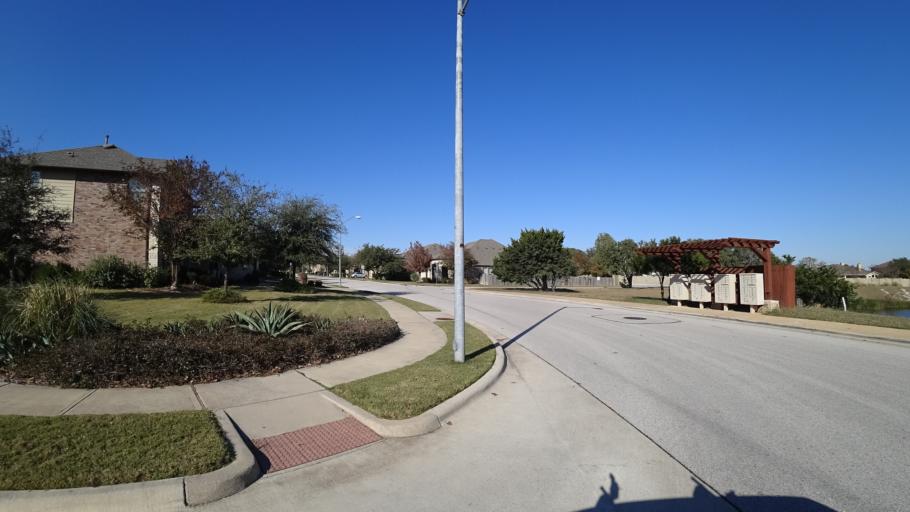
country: US
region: Texas
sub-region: Williamson County
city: Brushy Creek
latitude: 30.4875
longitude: -97.7218
